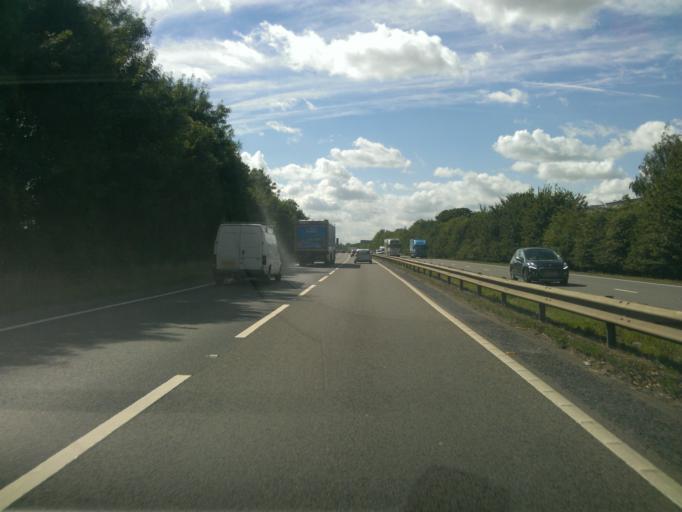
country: GB
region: England
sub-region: Northamptonshire
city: Thrapston
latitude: 52.3922
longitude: -0.5716
